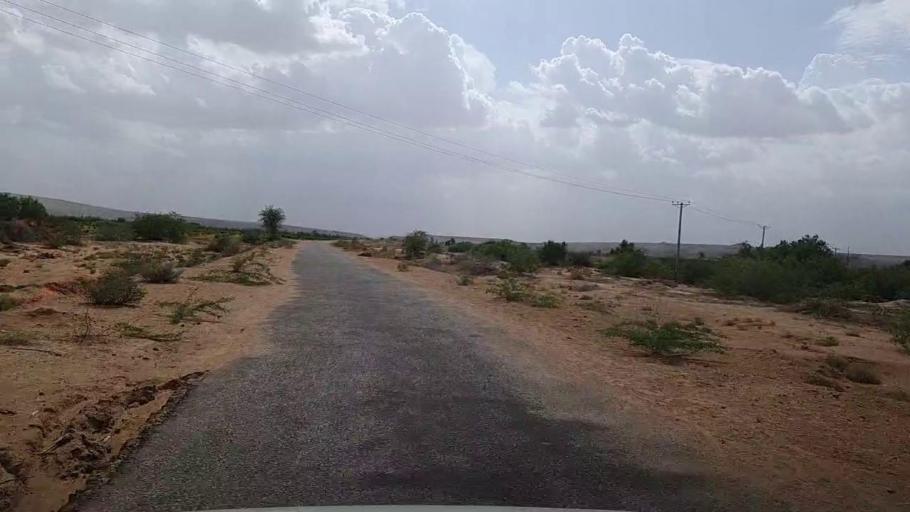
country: PK
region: Sindh
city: Jamshoro
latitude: 25.4036
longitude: 67.7796
